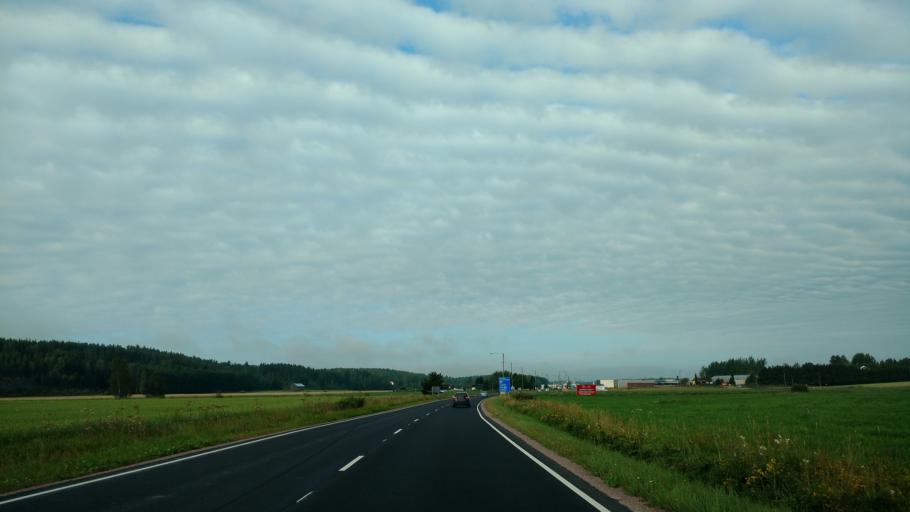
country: FI
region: Varsinais-Suomi
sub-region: Aboland-Turunmaa
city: Kimito
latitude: 60.1655
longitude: 22.7492
